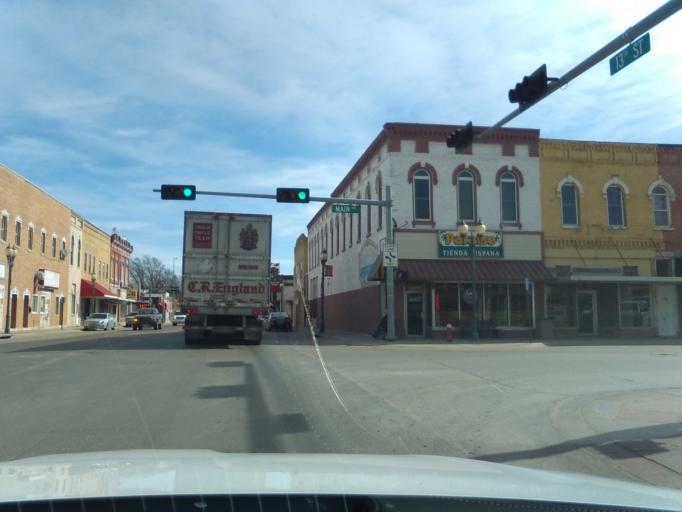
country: US
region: Nebraska
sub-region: Saline County
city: Crete
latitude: 40.6252
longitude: -96.9617
